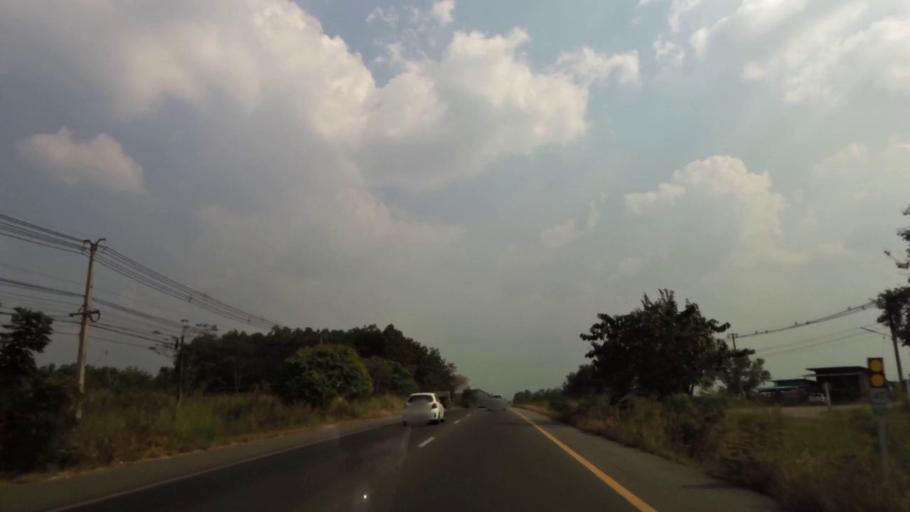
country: TH
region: Chon Buri
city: Nong Yai
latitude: 13.1426
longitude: 101.3390
